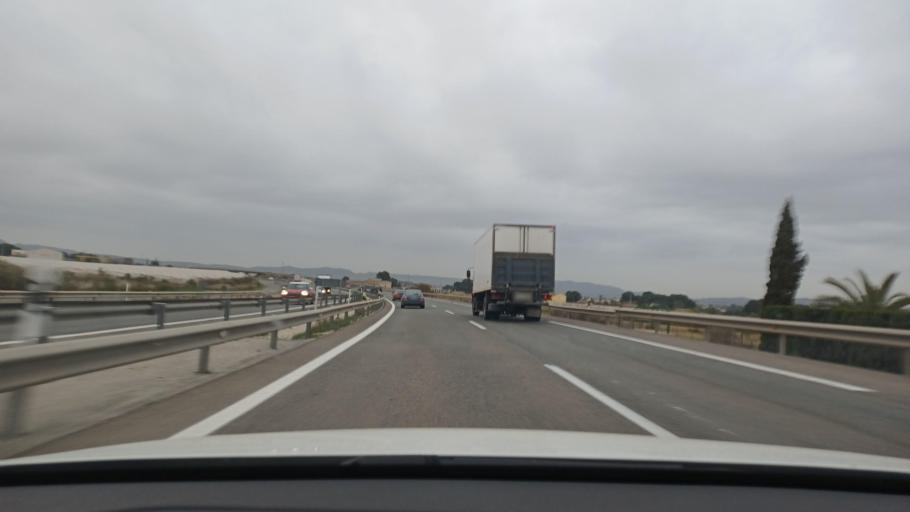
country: ES
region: Valencia
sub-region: Provincia de Alicante
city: Novelda
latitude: 38.4002
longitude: -0.7617
